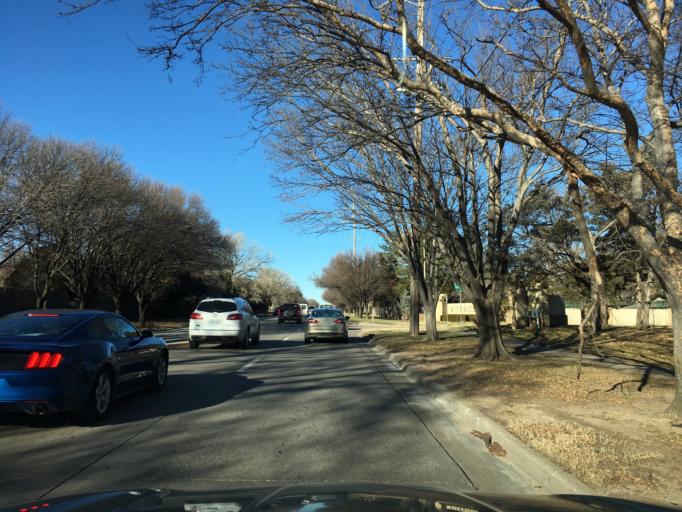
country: US
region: Kansas
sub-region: Sedgwick County
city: Bellaire
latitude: 37.6978
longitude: -97.2445
